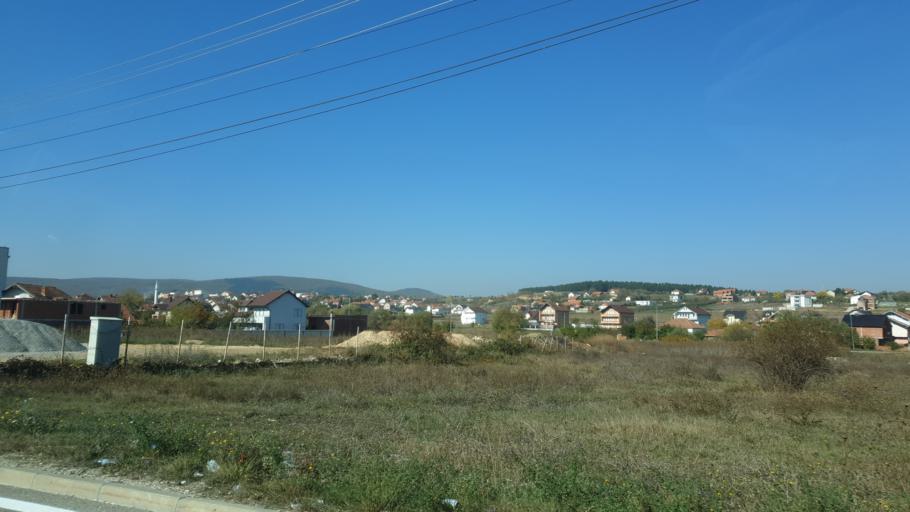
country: XK
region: Pristina
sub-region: Komuna e Gracanices
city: Glanica
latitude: 42.6007
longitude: 21.0264
